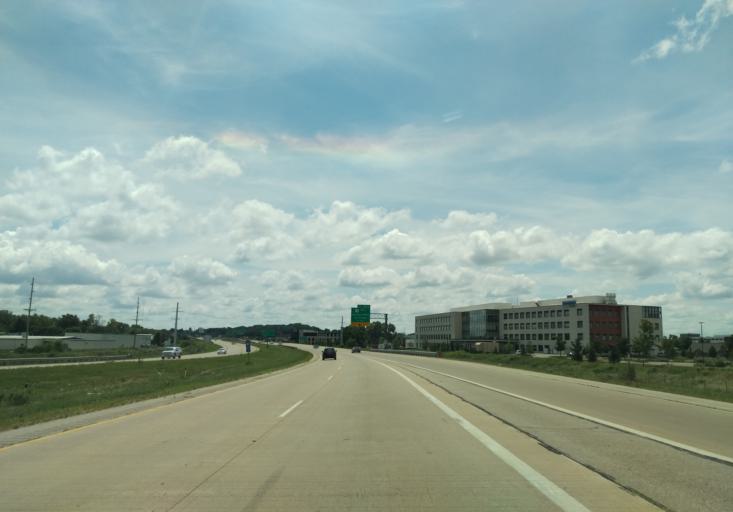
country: US
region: Wisconsin
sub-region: Dane County
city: Middleton
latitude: 43.1081
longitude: -89.5177
